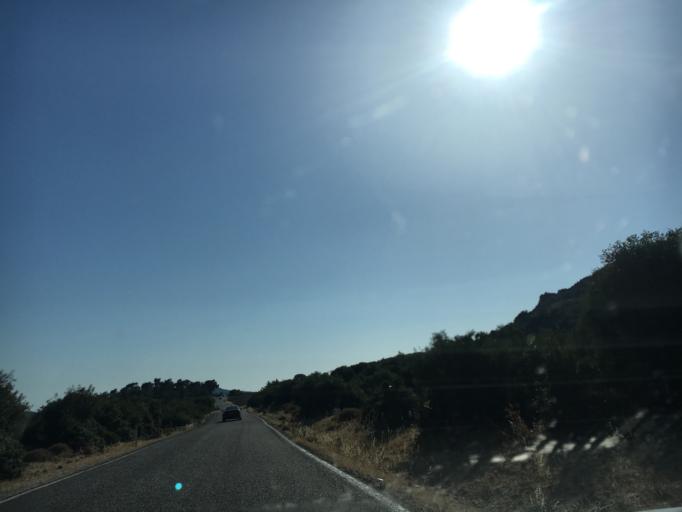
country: TR
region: Canakkale
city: Behram
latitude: 39.5066
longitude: 26.3736
